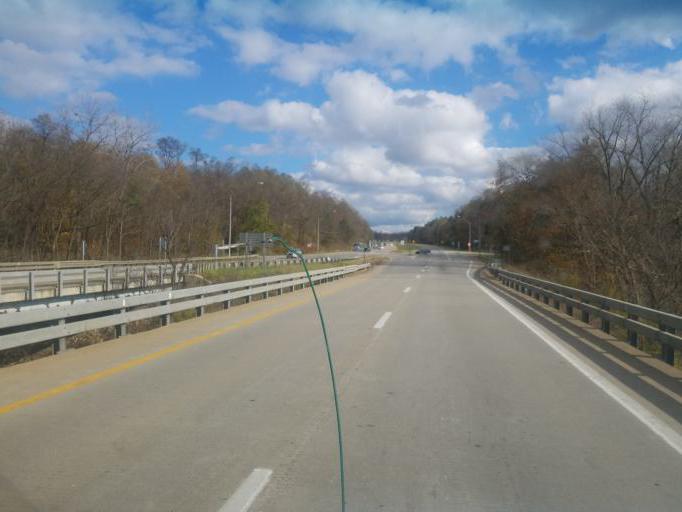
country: US
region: Ohio
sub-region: Richland County
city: Lincoln Heights
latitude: 40.7808
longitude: -82.3785
